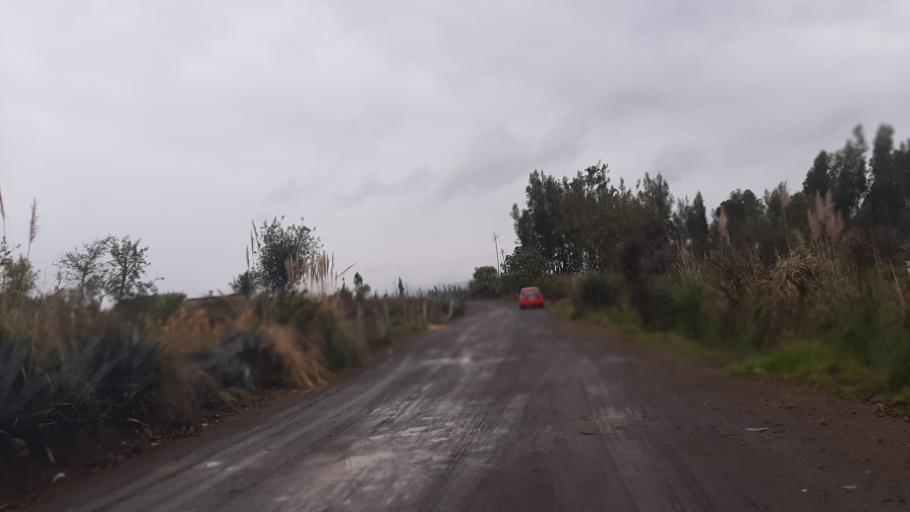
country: EC
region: Chimborazo
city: Riobamba
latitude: -1.6537
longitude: -78.6376
